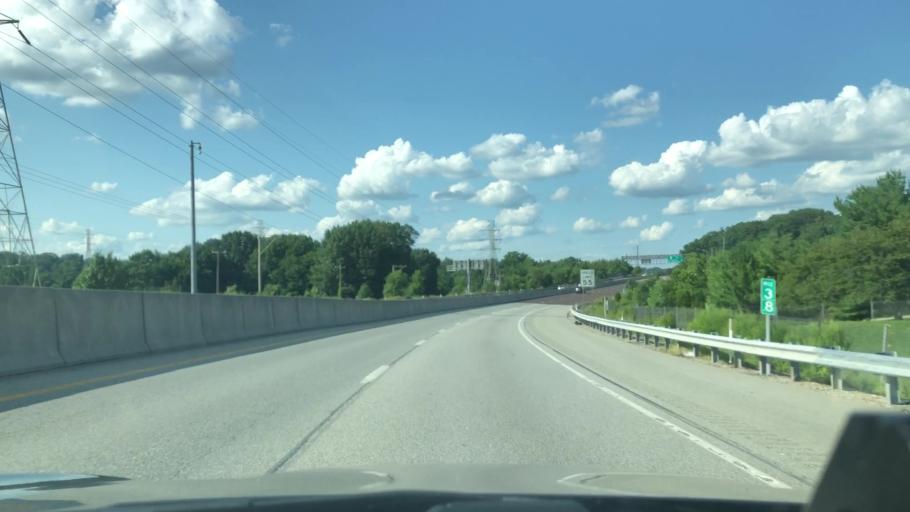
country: US
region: Pennsylvania
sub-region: Montgomery County
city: Fort Washington
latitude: 40.1229
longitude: -75.2048
